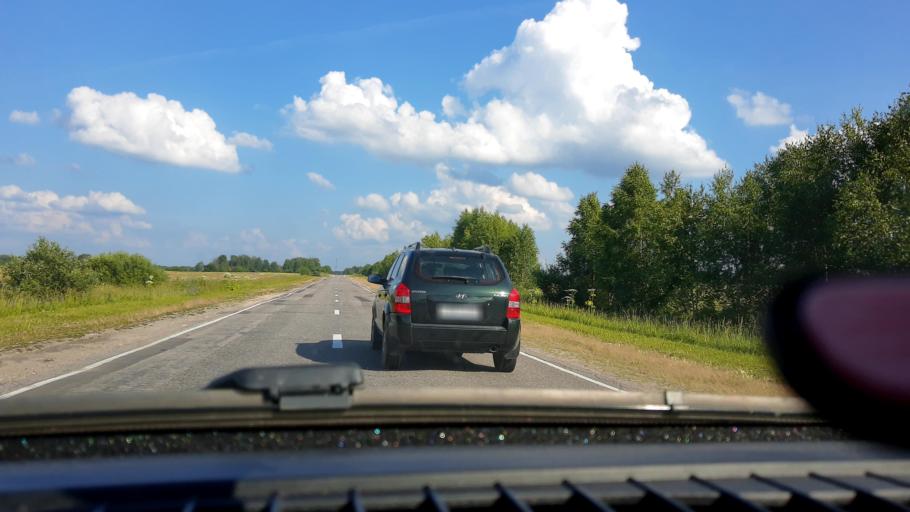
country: RU
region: Nizjnij Novgorod
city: Neklyudovo
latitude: 56.5016
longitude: 43.9875
